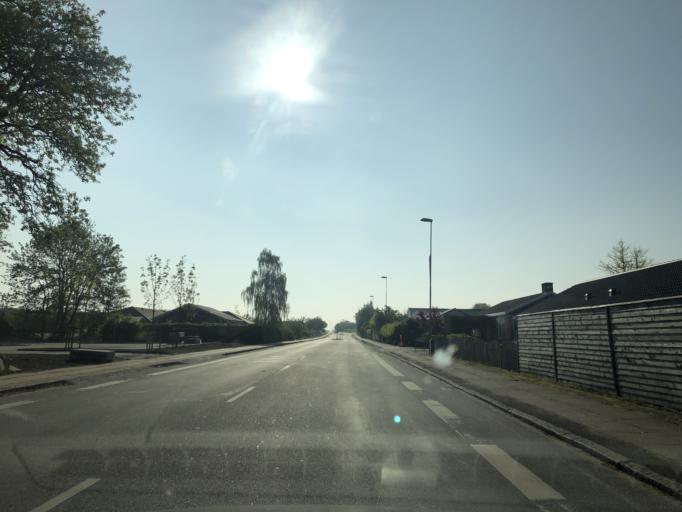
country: DK
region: Central Jutland
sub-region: Arhus Kommune
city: Solbjerg
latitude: 56.0450
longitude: 10.0867
